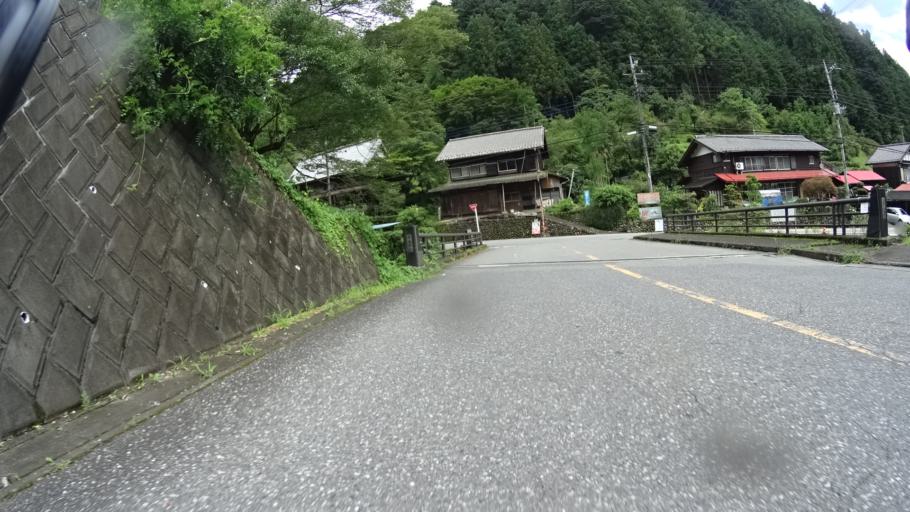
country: JP
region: Tokyo
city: Ome
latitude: 35.8347
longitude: 139.2085
